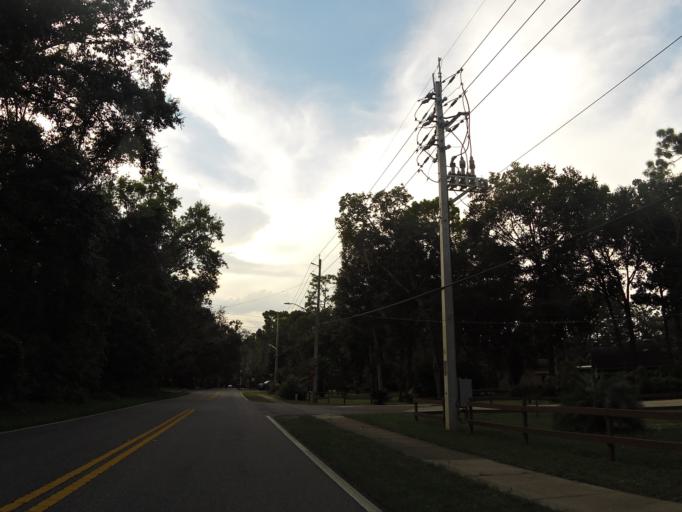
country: US
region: Florida
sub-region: Saint Johns County
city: Fruit Cove
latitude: 30.1392
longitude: -81.6107
